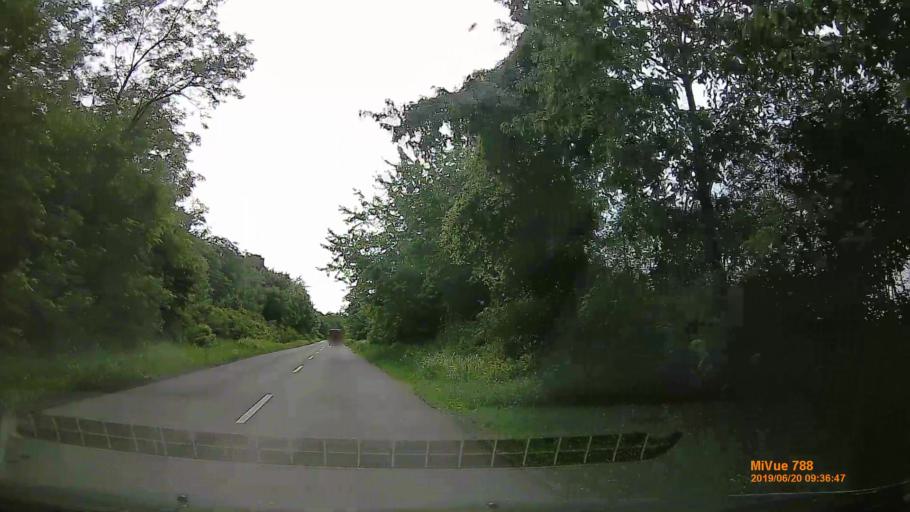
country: HU
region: Baranya
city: Pecsvarad
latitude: 46.1682
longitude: 18.4558
